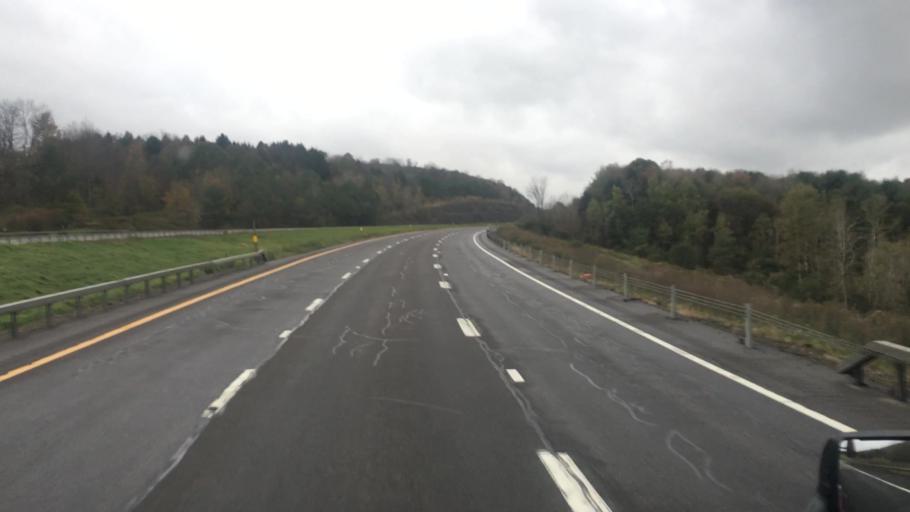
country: US
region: New York
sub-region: Chenango County
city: Greene
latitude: 42.1893
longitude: -75.6516
